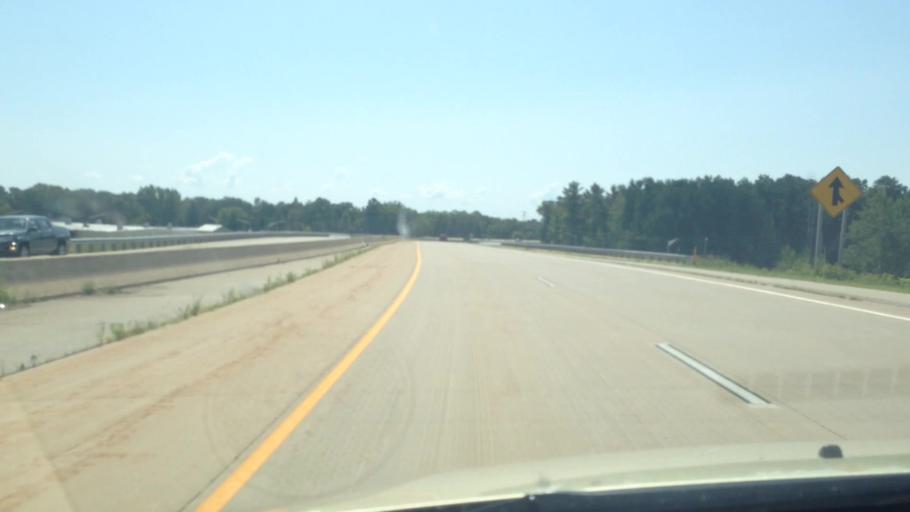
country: US
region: Wisconsin
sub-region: Oconto County
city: Oconto
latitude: 44.8938
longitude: -87.8986
